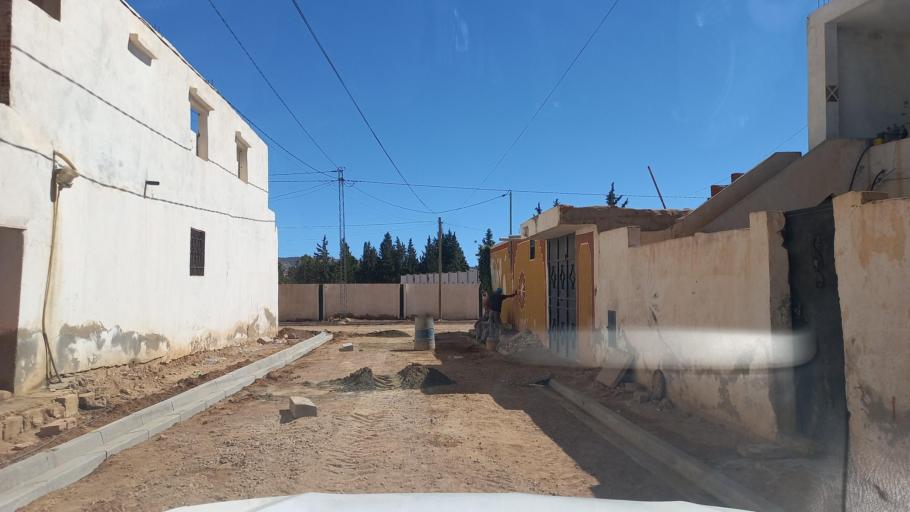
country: TN
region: Al Qasrayn
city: Sbiba
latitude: 35.3596
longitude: 9.0905
